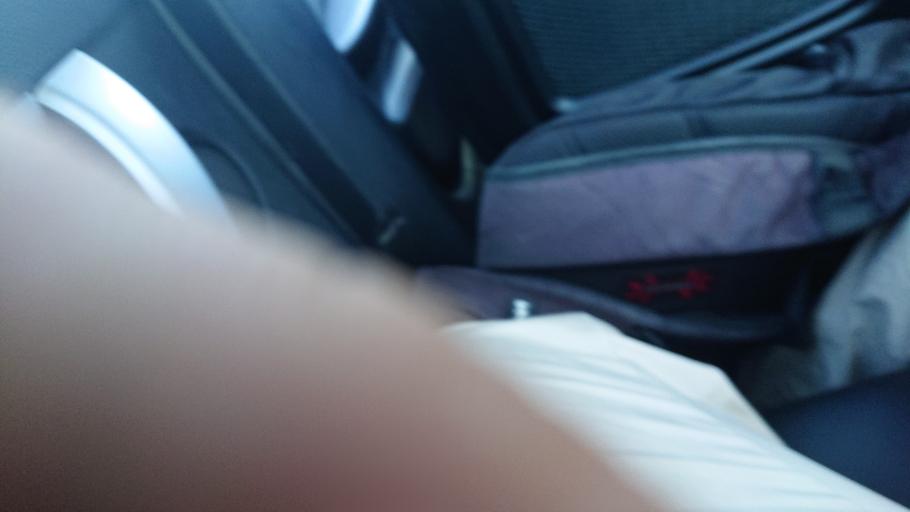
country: TW
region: Taiwan
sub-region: Chiayi
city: Taibao
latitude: 23.7116
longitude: 120.1890
